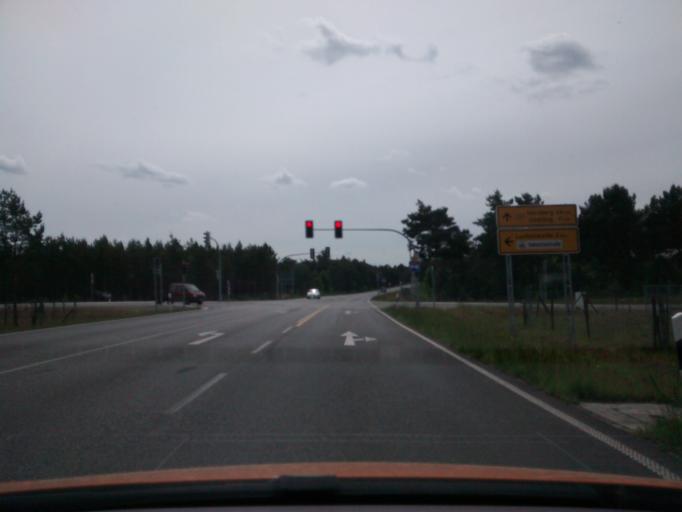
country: DE
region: Brandenburg
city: Luckenwalde
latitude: 52.0801
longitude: 13.1312
